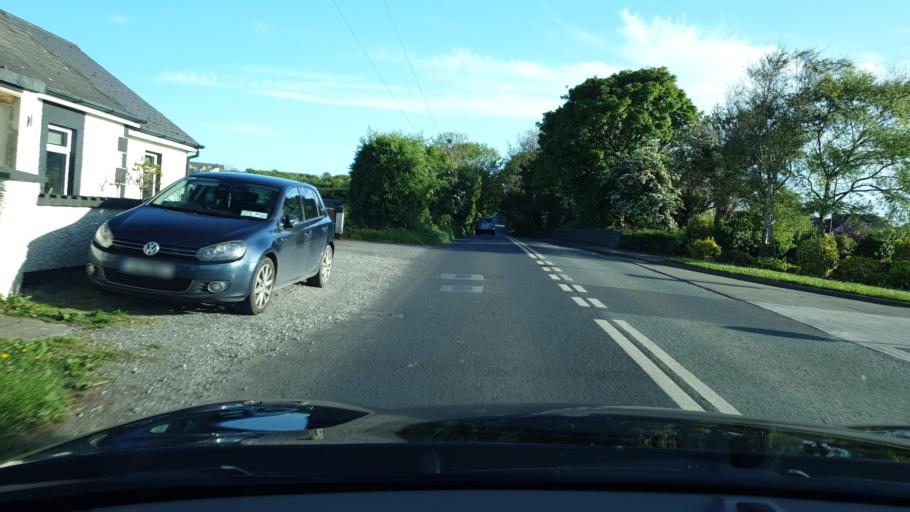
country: IE
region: Leinster
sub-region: Fingal County
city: Skerries
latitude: 53.5655
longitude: -6.1026
